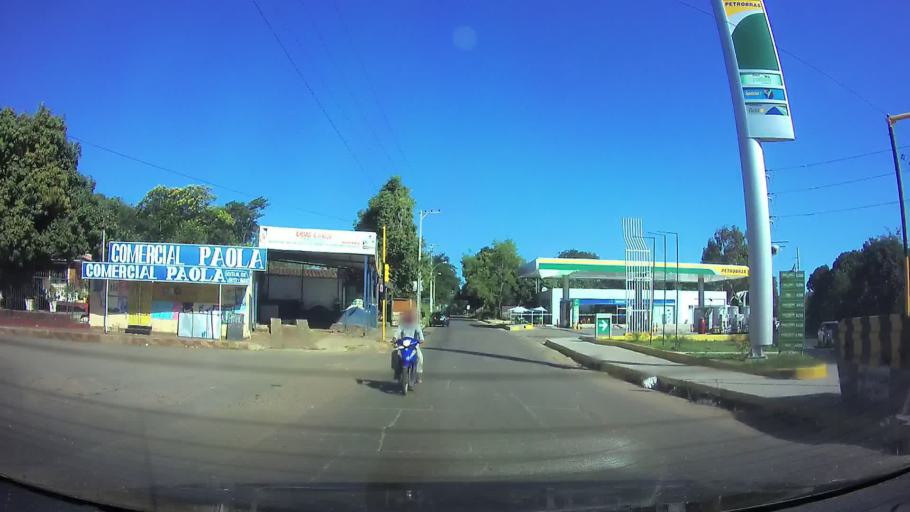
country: PY
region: Central
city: Fernando de la Mora
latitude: -25.2959
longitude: -57.5358
